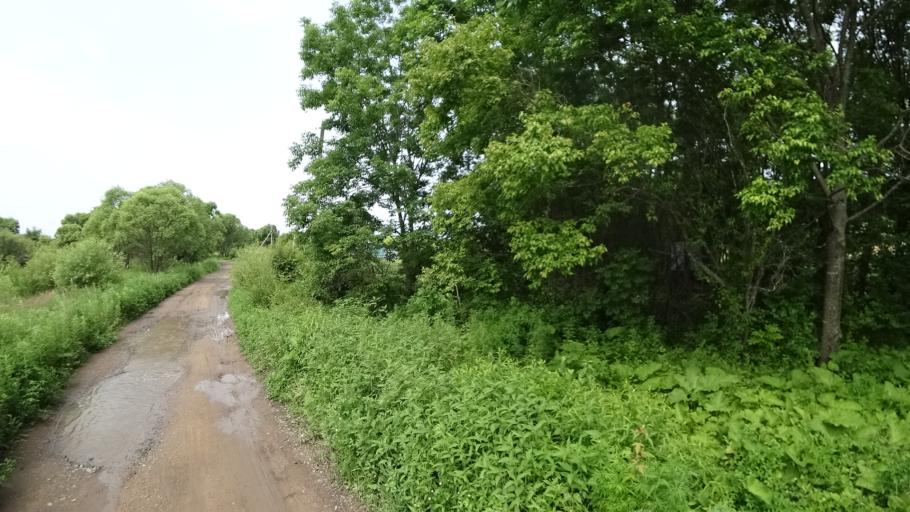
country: RU
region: Primorskiy
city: Novosysoyevka
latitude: 44.2478
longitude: 133.3707
